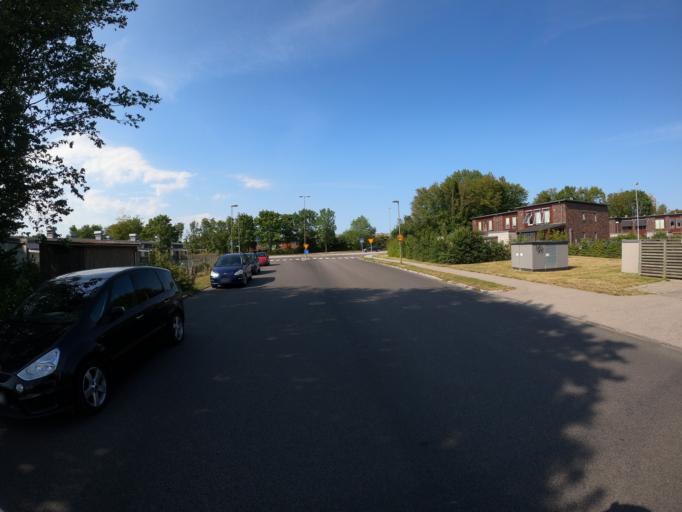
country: SE
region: Skane
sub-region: Lunds Kommun
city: Lund
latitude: 55.7232
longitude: 13.1796
